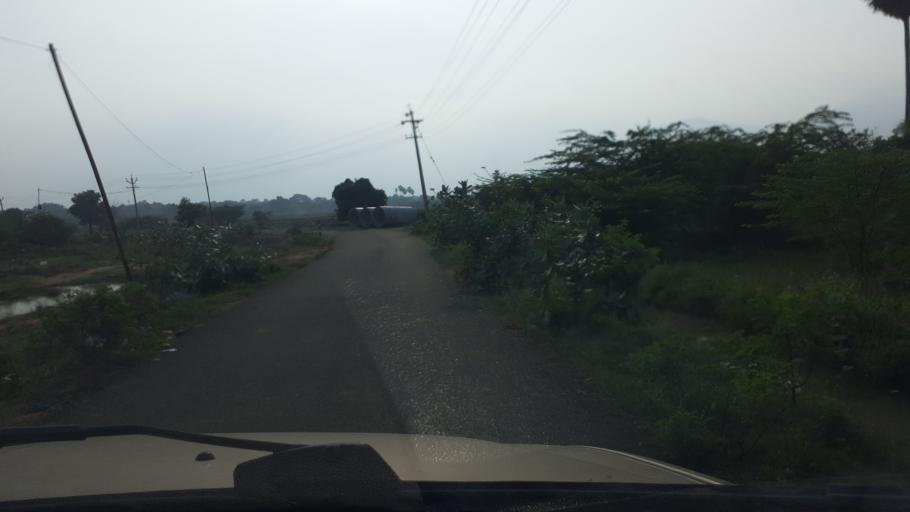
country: IN
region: Tamil Nadu
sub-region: Tirunelveli Kattabo
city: Kalakkadu
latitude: 8.4727
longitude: 77.5868
